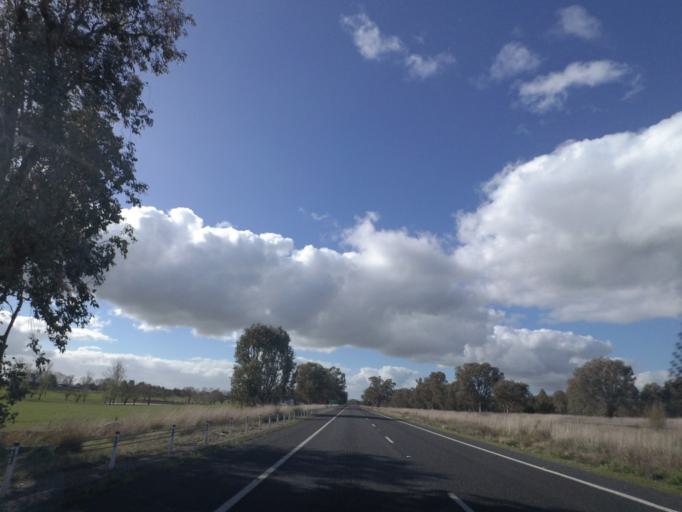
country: AU
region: New South Wales
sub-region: Greater Hume Shire
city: Holbrook
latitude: -35.7541
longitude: 147.2938
